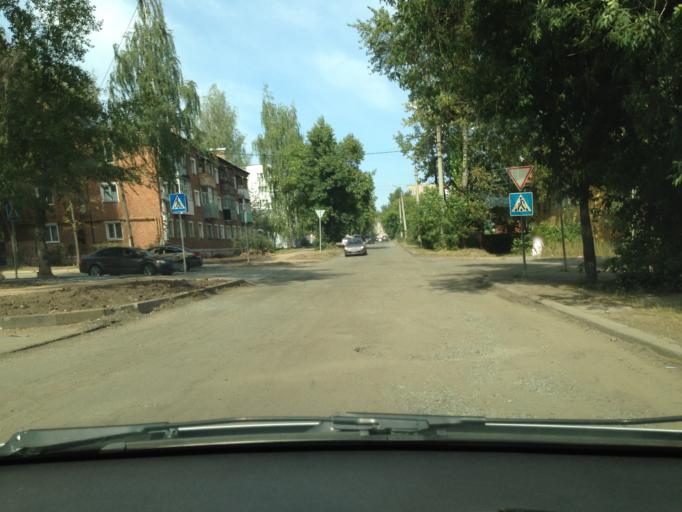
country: RU
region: Udmurtiya
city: Izhevsk
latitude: 56.8729
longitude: 53.1894
